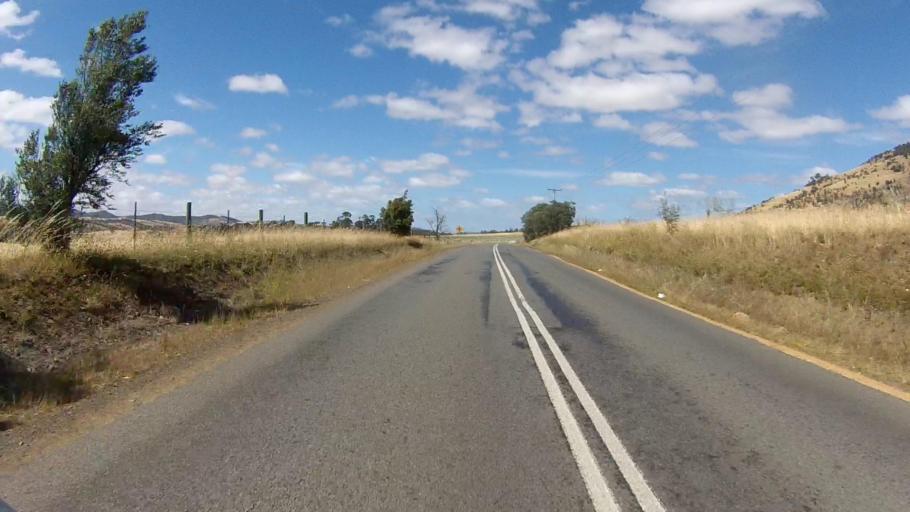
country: AU
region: Tasmania
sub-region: Sorell
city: Sorell
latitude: -42.6314
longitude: 147.4295
